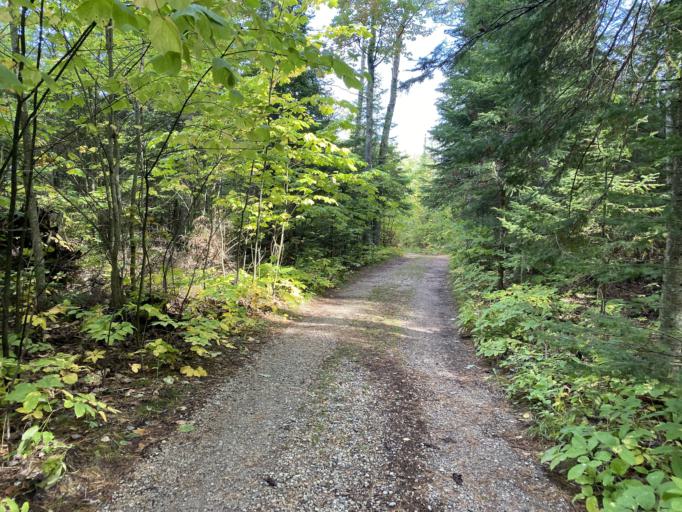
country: US
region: Michigan
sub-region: Mackinac County
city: Saint Ignace
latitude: 45.7504
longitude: -84.8781
